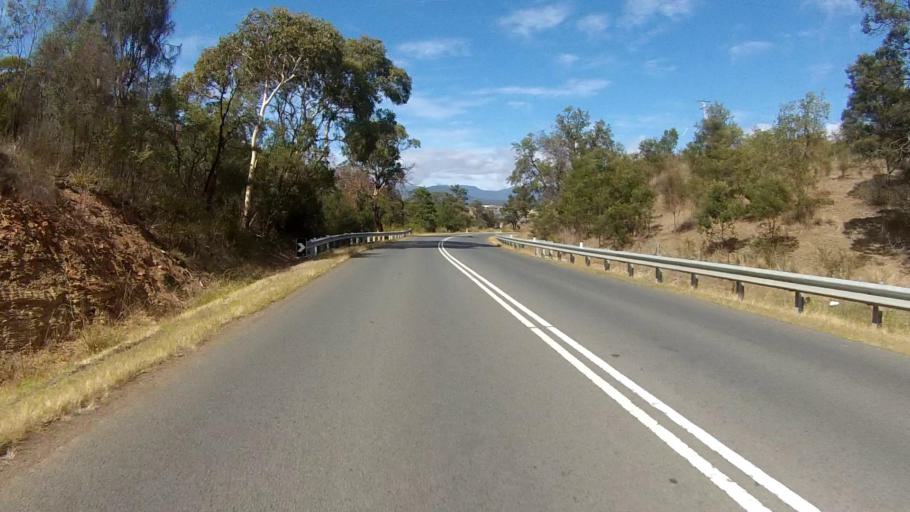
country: AU
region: Tasmania
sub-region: Brighton
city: Old Beach
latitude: -42.7437
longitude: 147.2836
